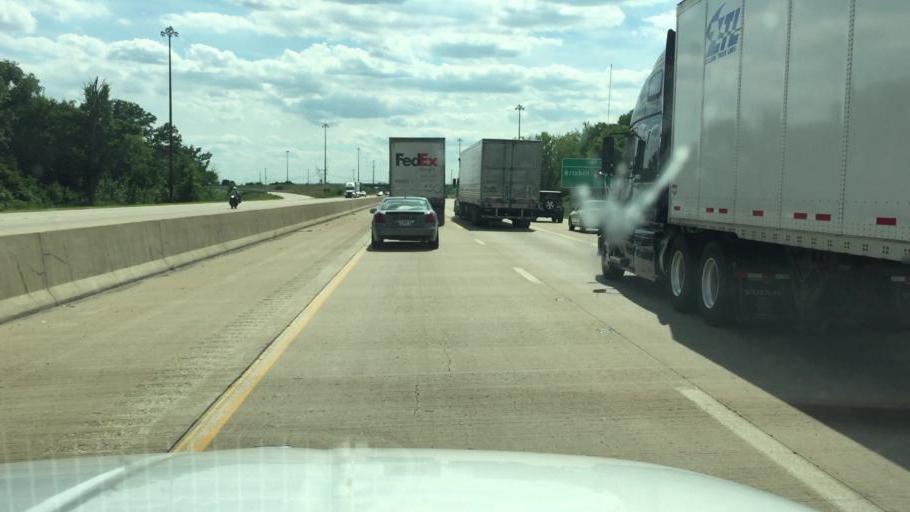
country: US
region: Illinois
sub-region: Grundy County
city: Morris
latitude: 41.4250
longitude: -88.3584
